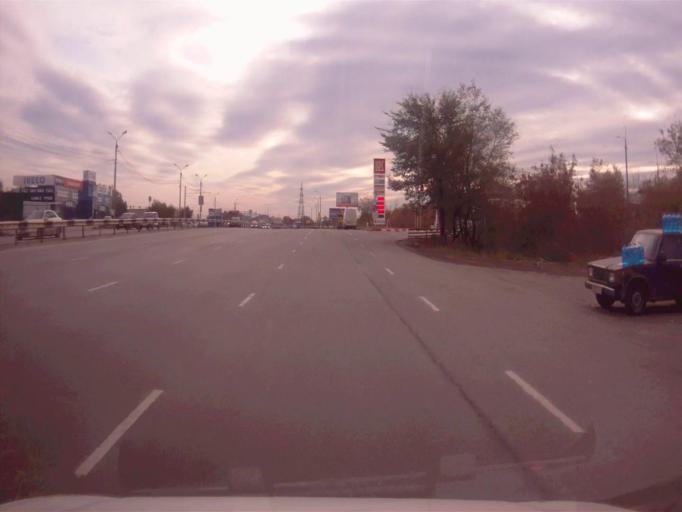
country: RU
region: Chelyabinsk
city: Novosineglazovskiy
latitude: 55.0765
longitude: 61.3882
